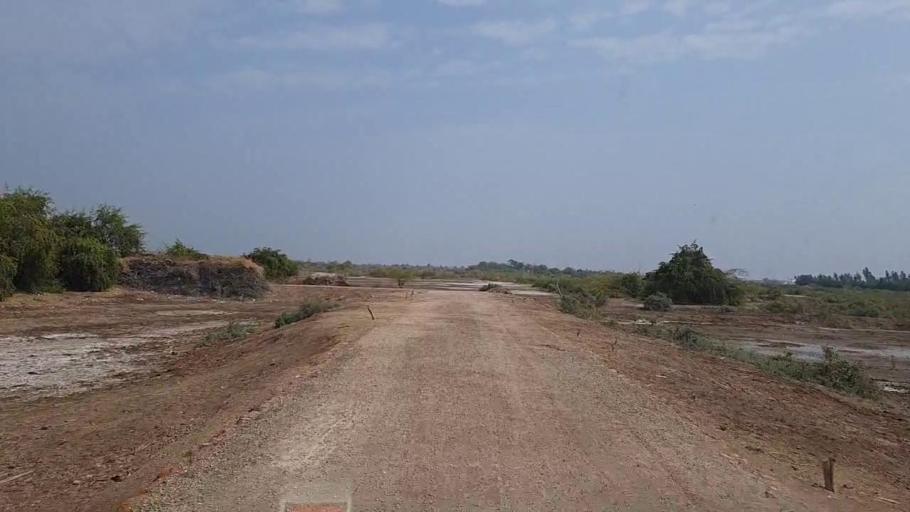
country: PK
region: Sindh
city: Mirwah Gorchani
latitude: 25.3406
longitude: 69.0431
